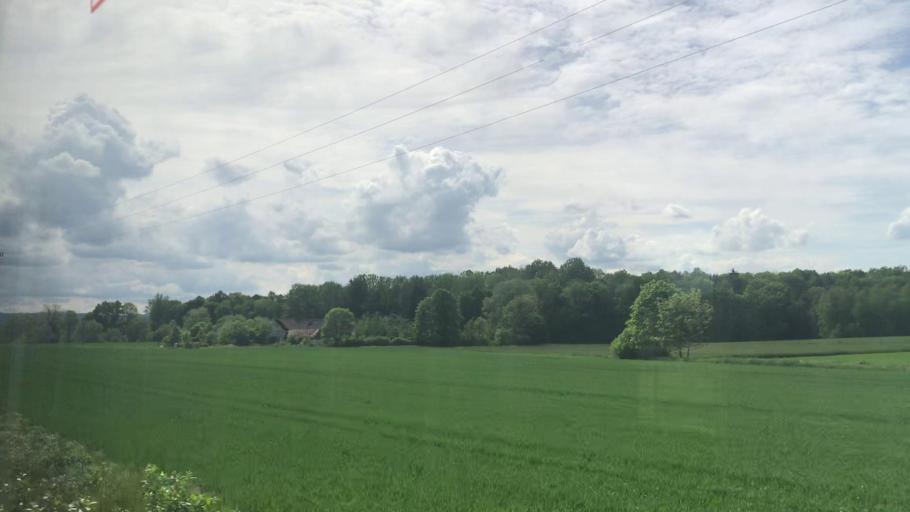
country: PL
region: Lower Silesian Voivodeship
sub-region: Powiat swidnicki
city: Jaworzyna Slaska
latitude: 50.8996
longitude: 16.4079
